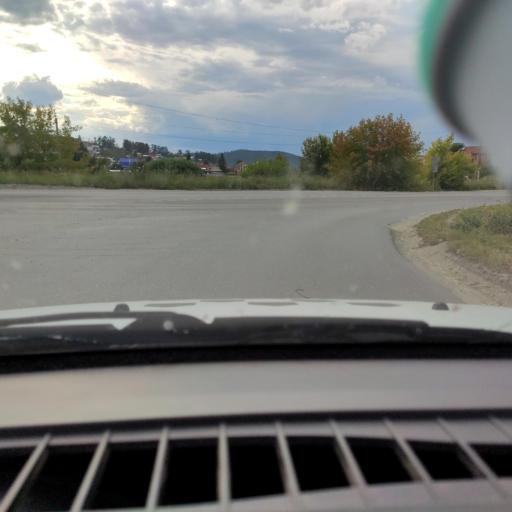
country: RU
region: Chelyabinsk
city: Miass
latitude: 55.0646
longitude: 60.1008
